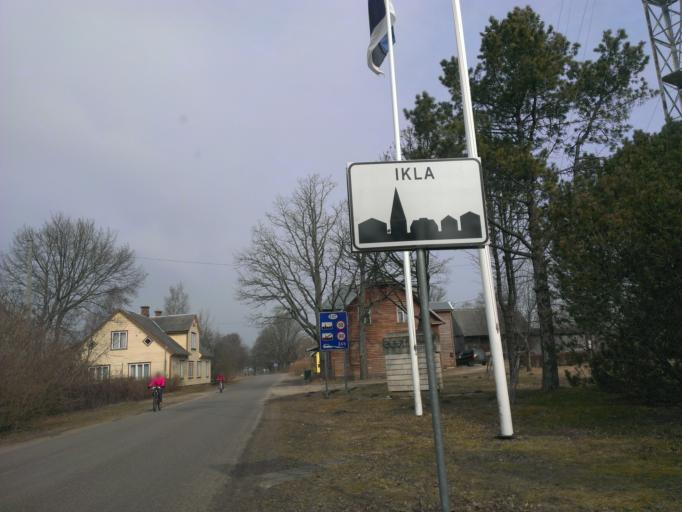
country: LV
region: Salacgrivas
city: Ainazi
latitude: 57.8747
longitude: 24.3613
